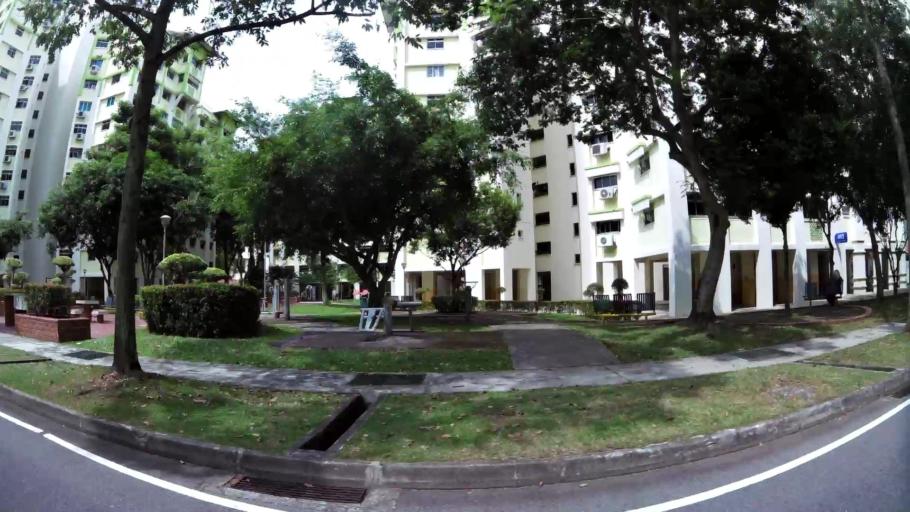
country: MY
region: Johor
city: Johor Bahru
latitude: 1.4277
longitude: 103.7740
